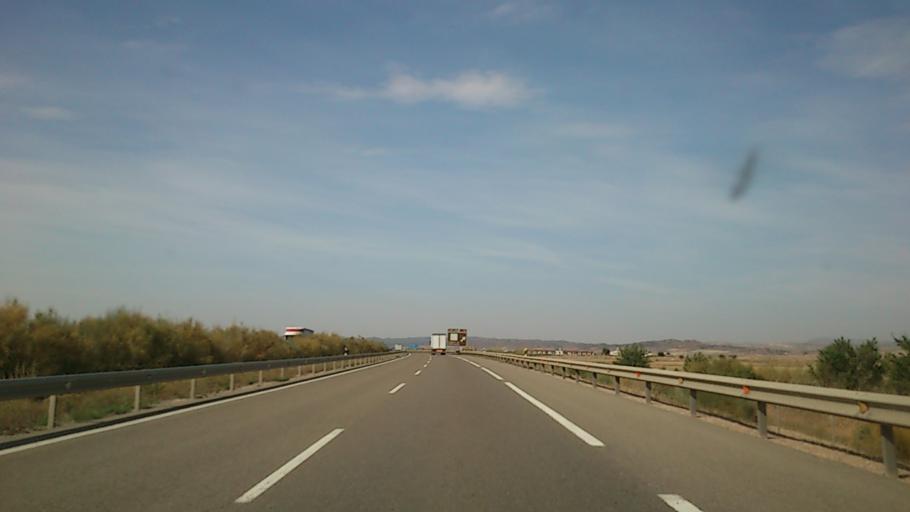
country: ES
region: Aragon
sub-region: Provincia de Teruel
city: Fuentes Claras
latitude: 40.8653
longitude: -1.3075
